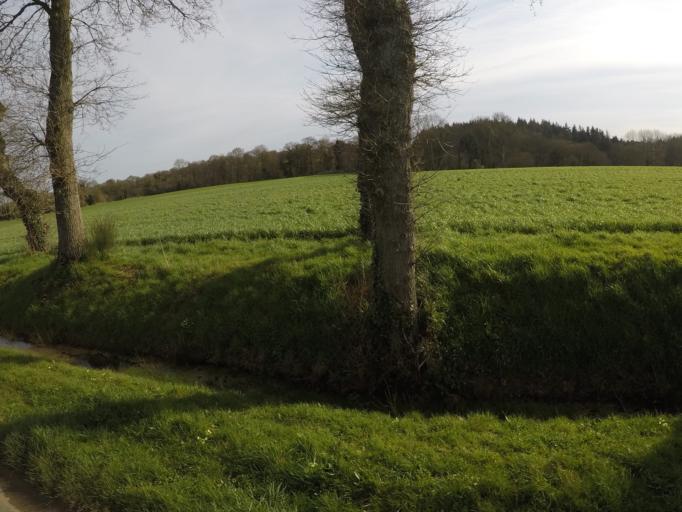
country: FR
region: Brittany
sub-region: Departement des Cotes-d'Armor
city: Plelo
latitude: 48.5336
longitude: -2.9683
